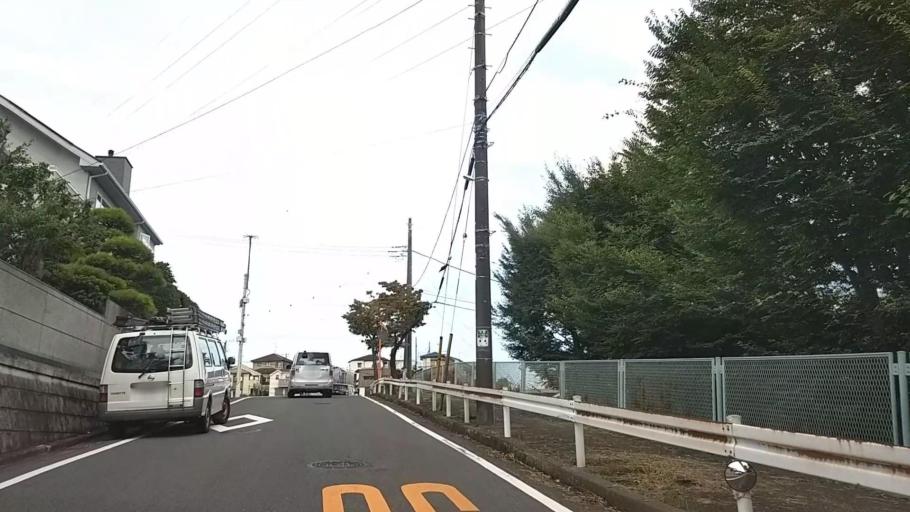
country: JP
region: Kanagawa
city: Yokohama
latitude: 35.4808
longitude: 139.5630
